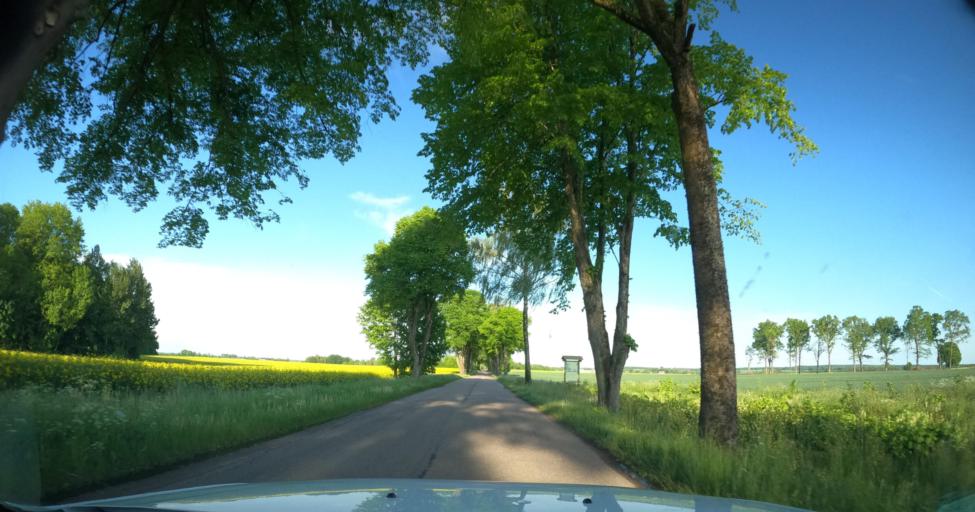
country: PL
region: Warmian-Masurian Voivodeship
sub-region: Powiat braniewski
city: Braniewo
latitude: 54.2803
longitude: 19.9051
